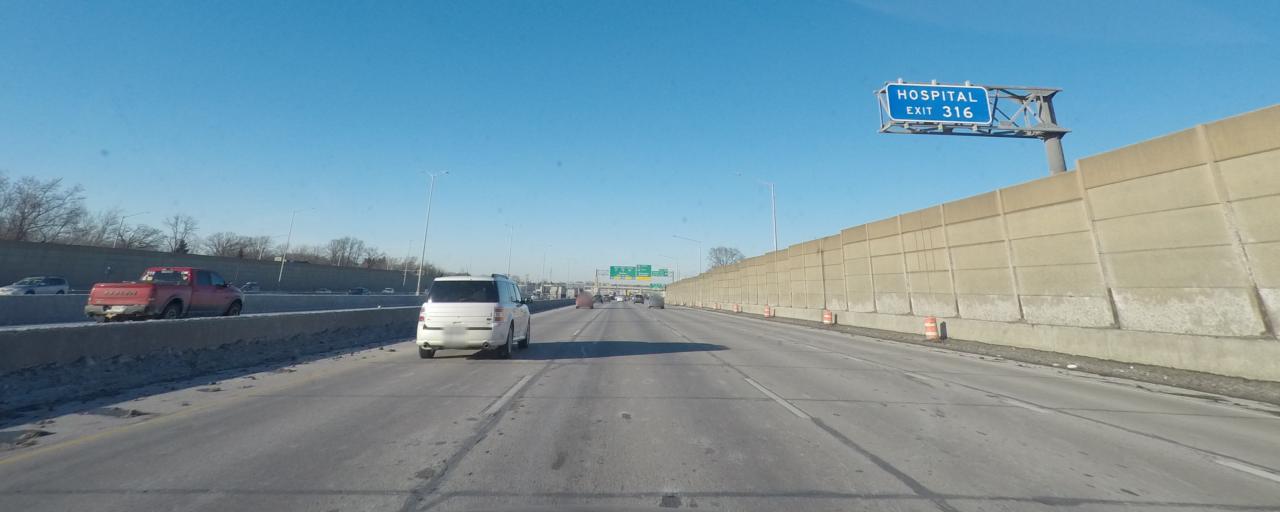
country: US
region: Wisconsin
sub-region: Milwaukee County
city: Saint Francis
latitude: 42.9550
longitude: -87.9326
